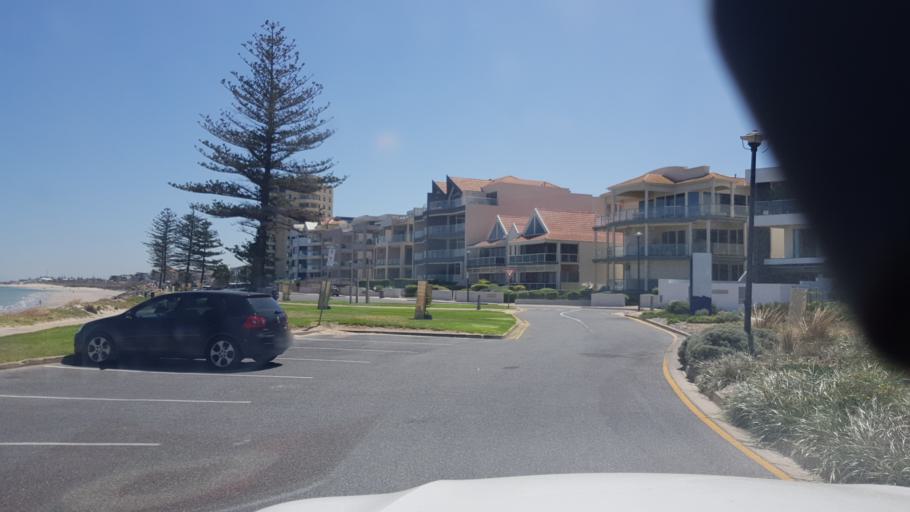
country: AU
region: South Australia
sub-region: Adelaide
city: Glenelg
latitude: -34.9738
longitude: 138.5111
